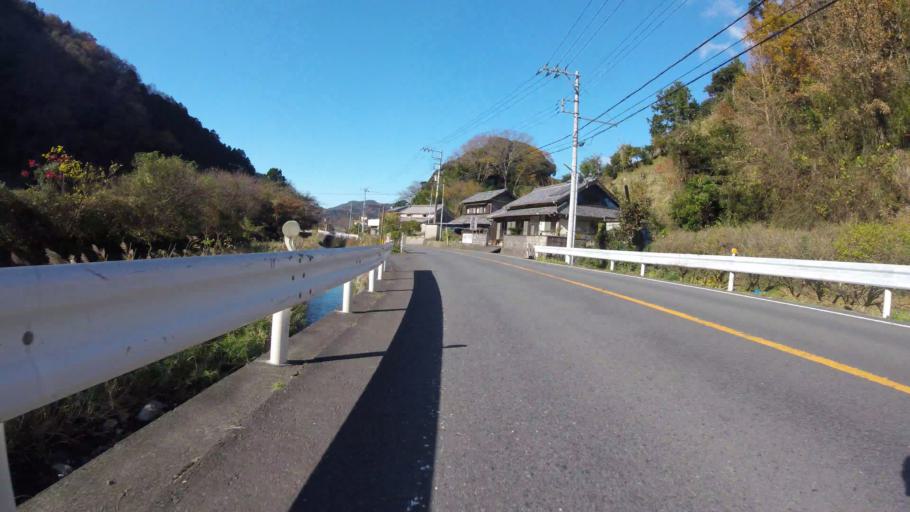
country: JP
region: Shizuoka
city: Shimoda
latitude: 34.7559
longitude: 138.8285
